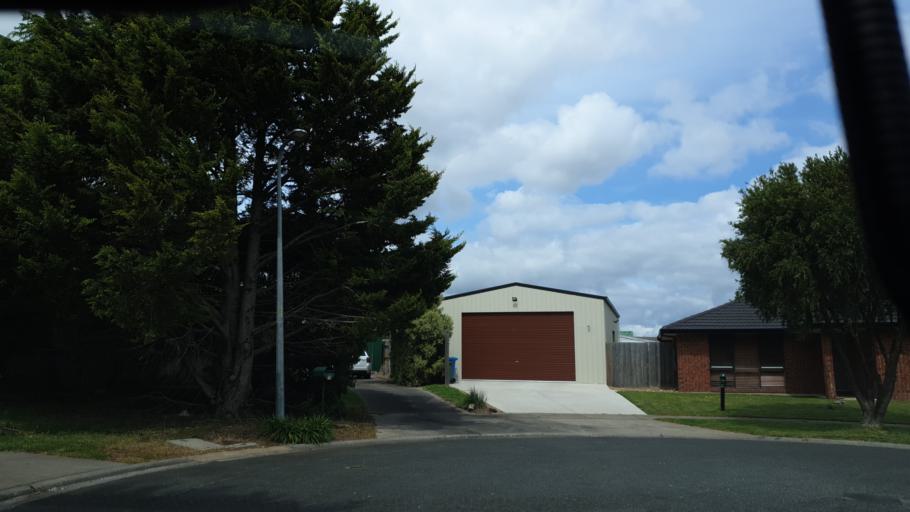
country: AU
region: Victoria
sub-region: Casey
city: Cranbourne North
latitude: -38.0796
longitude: 145.2788
